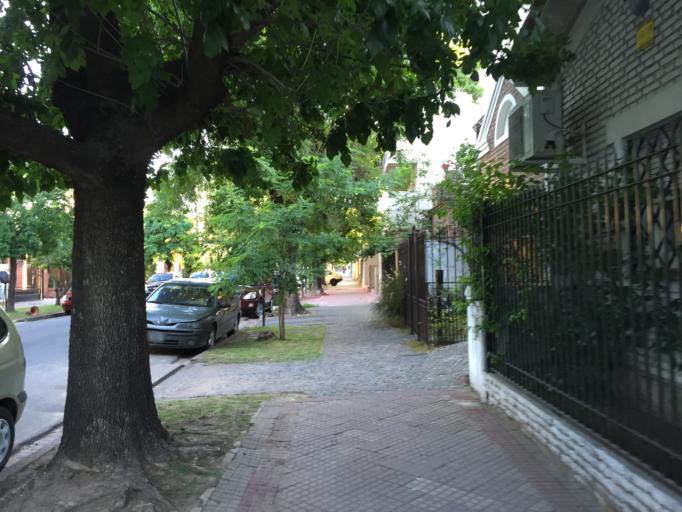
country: AR
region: Buenos Aires
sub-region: Partido de Lomas de Zamora
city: Lomas de Zamora
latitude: -34.7592
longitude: -58.3946
